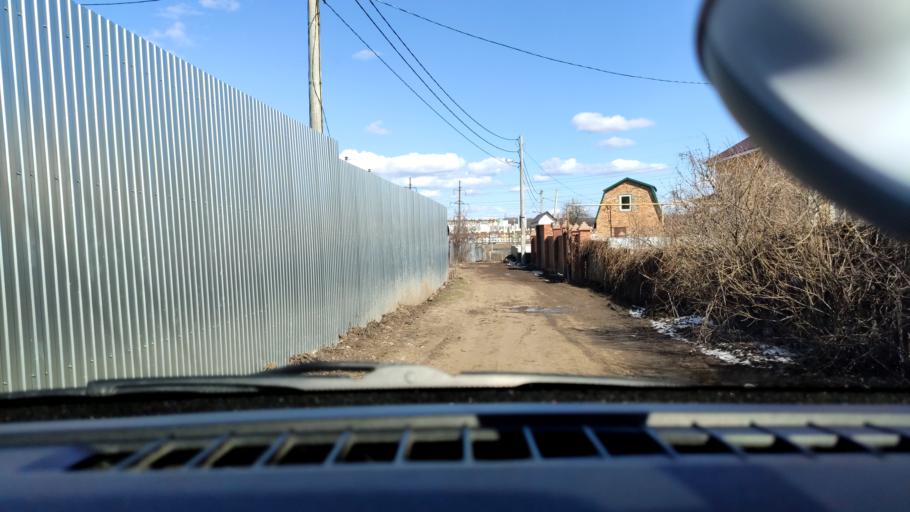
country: RU
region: Samara
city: Petra-Dubrava
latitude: 53.2917
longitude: 50.3117
